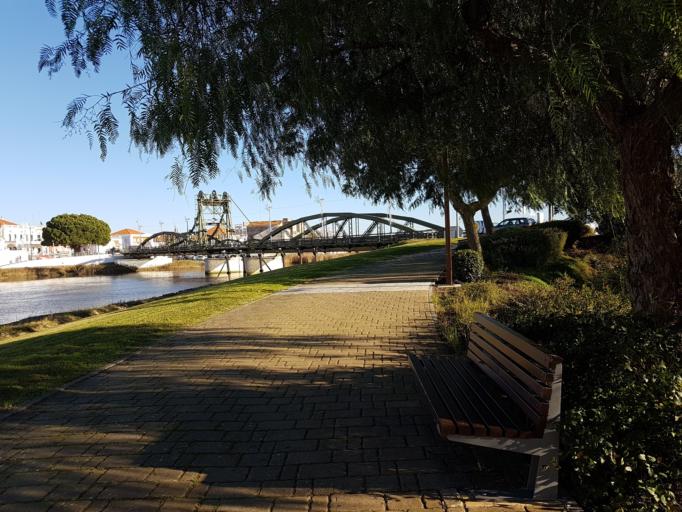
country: PT
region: Setubal
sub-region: Alcacer do Sal
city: Alcacer do Sal
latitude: 38.3703
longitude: -8.5082
